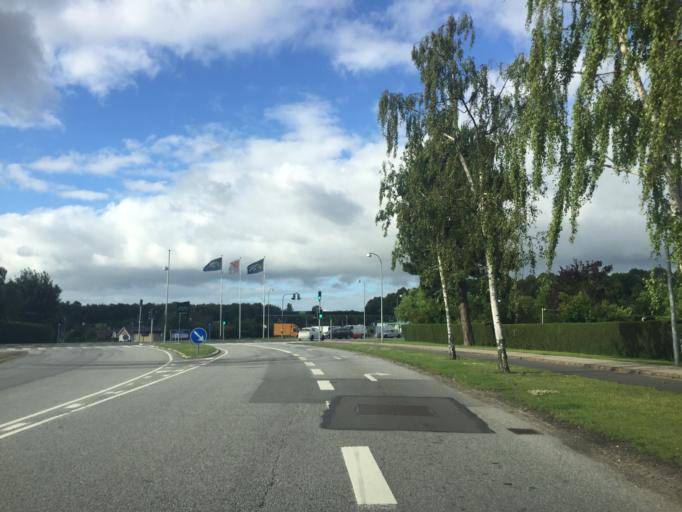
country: DK
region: Capital Region
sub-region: Brondby Kommune
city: Brondbyvester
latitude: 55.6551
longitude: 12.4288
